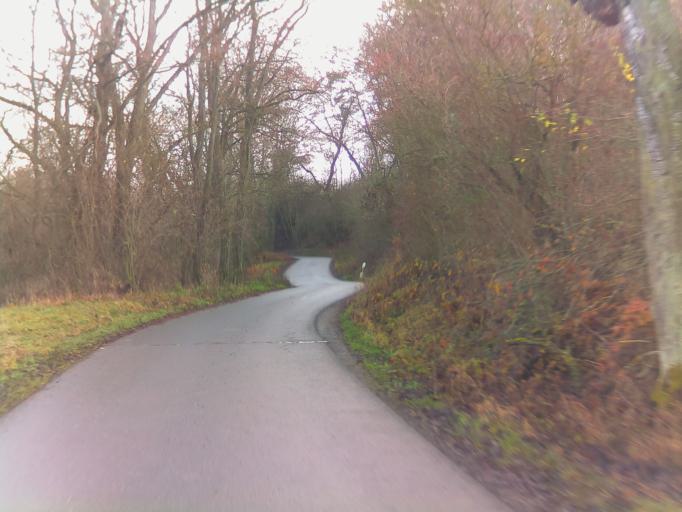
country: DE
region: Thuringia
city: Gumperda
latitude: 50.8023
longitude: 11.5132
